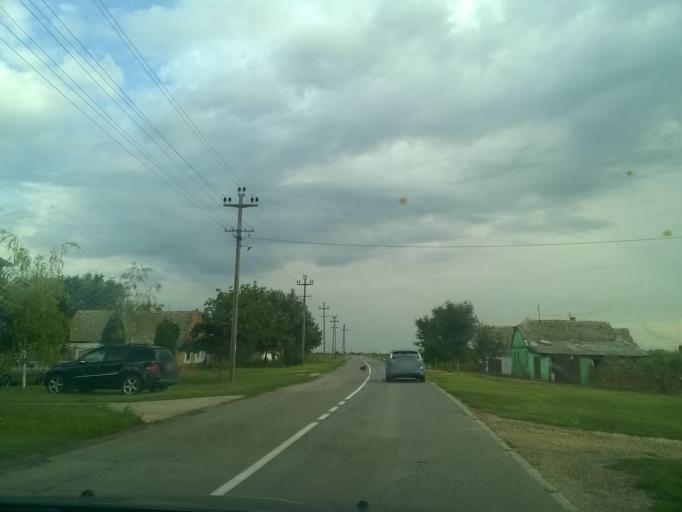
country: RS
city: Uzdin
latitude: 45.2129
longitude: 20.6302
